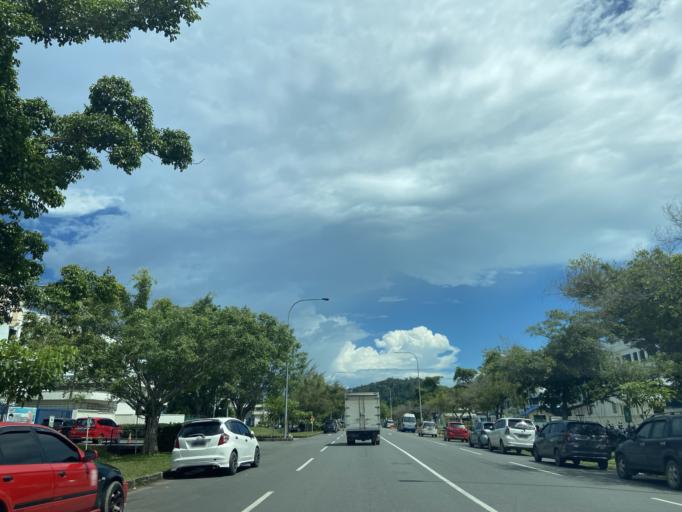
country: SG
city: Singapore
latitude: 1.0621
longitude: 104.0348
